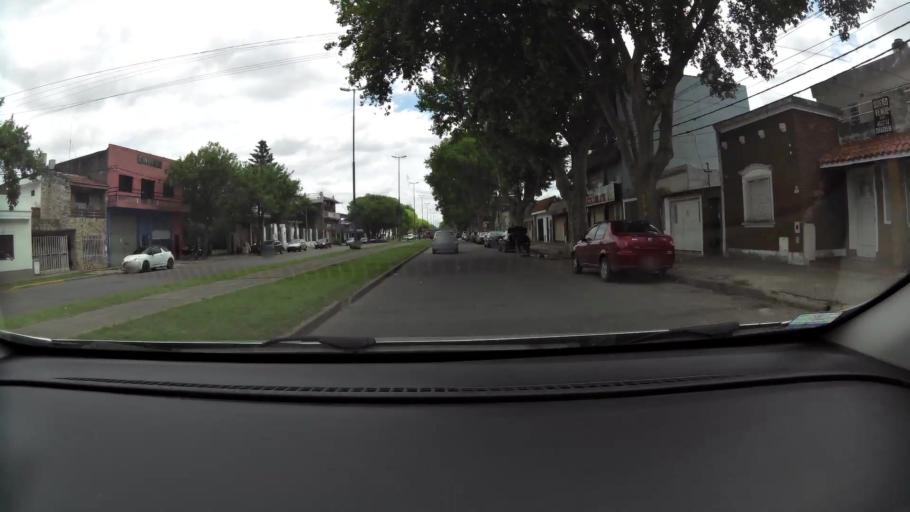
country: AR
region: Santa Fe
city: Gobernador Galvez
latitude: -32.9905
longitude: -60.6407
